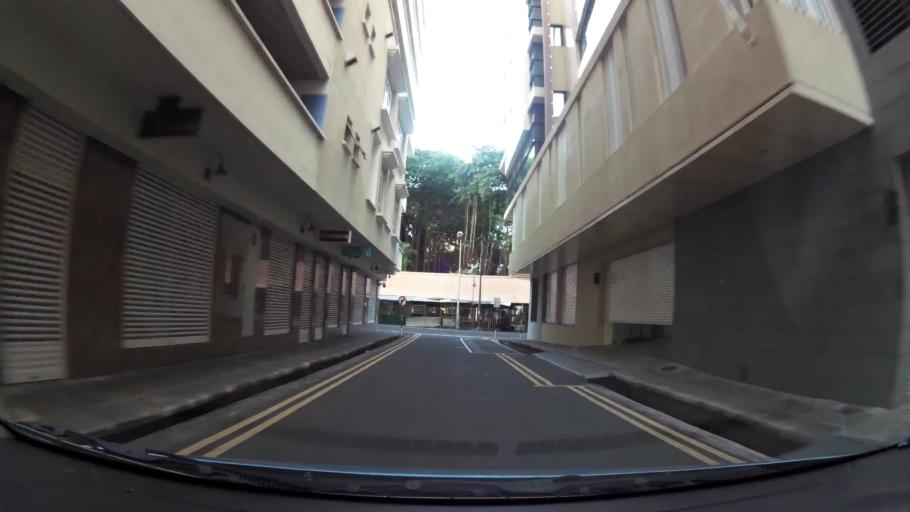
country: MU
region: Port Louis
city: Port Louis
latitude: -20.1640
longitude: 57.5013
